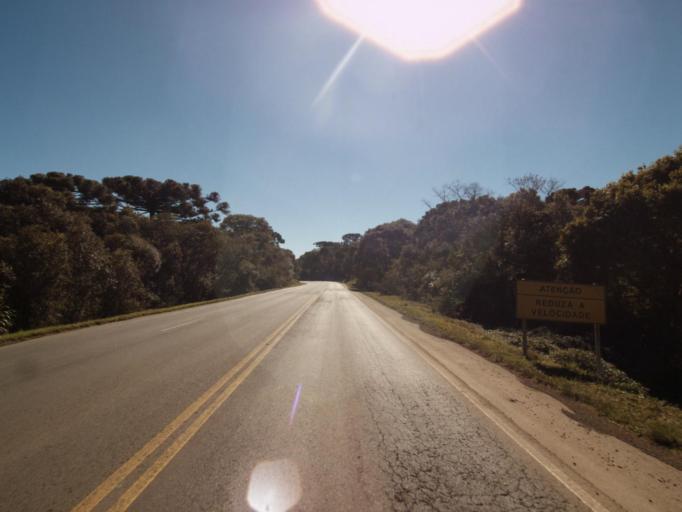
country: BR
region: Santa Catarina
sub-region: Joacaba
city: Joacaba
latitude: -27.0886
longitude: -51.6614
